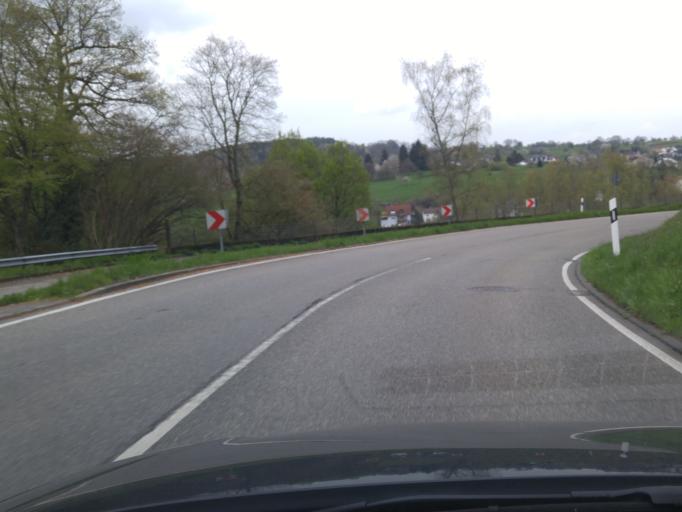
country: DE
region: Hesse
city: Neckarsteinach
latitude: 49.3933
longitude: 8.8496
